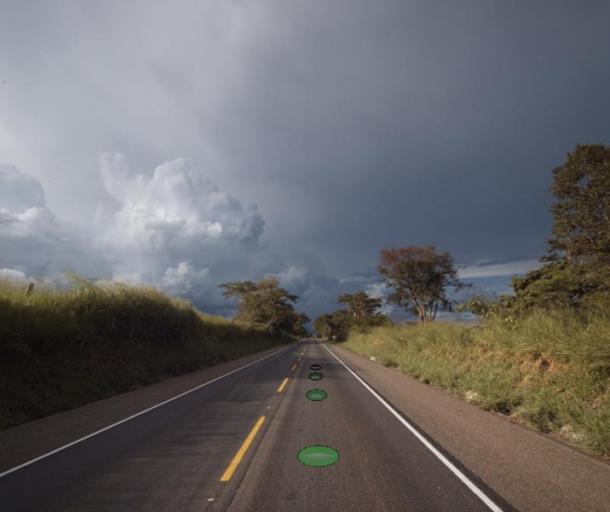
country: BR
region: Goias
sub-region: Ceres
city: Ceres
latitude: -15.1653
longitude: -49.5419
